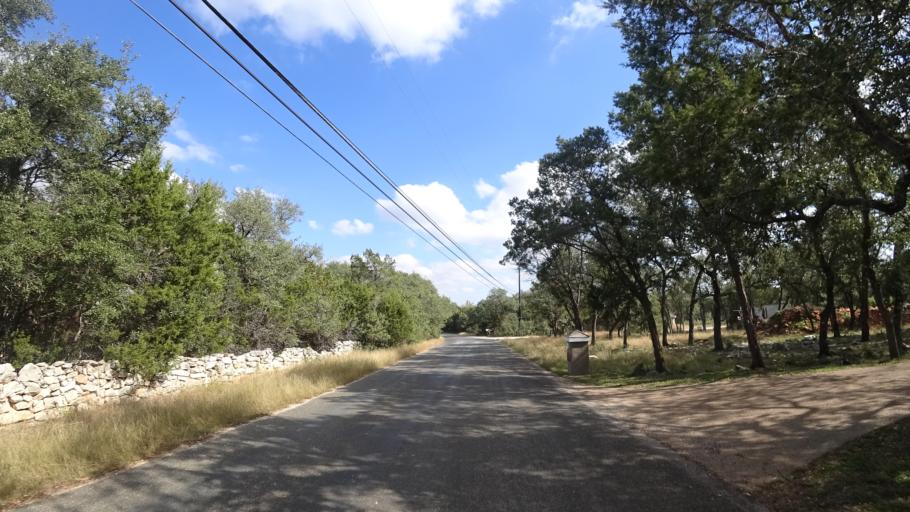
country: US
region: Texas
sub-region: Travis County
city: Shady Hollow
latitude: 30.1758
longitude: -97.8641
